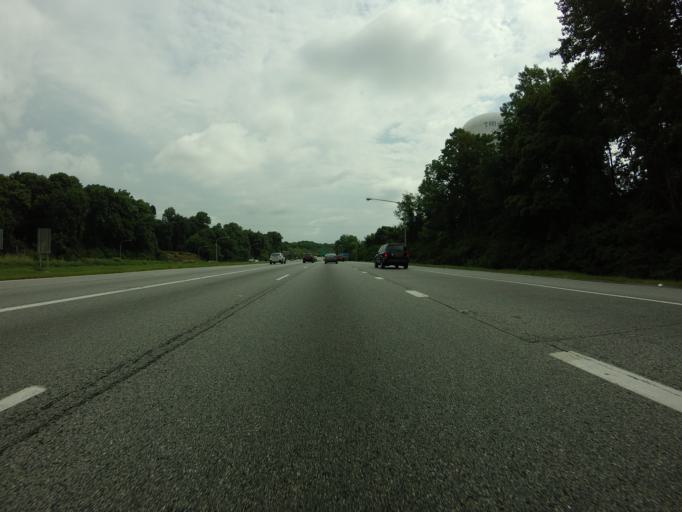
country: US
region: Pennsylvania
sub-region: Delaware County
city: Boothwyn
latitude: 39.8181
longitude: -75.4504
